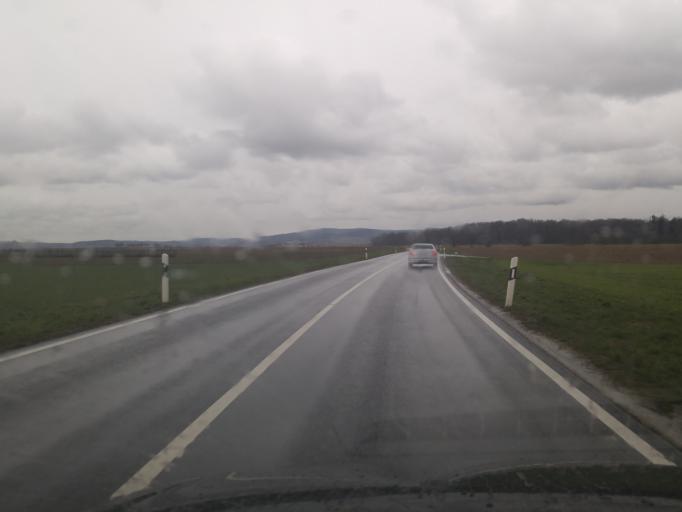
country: DE
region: Baden-Wuerttemberg
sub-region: Regierungsbezirk Stuttgart
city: Affalterbach
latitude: 48.9121
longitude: 9.3375
